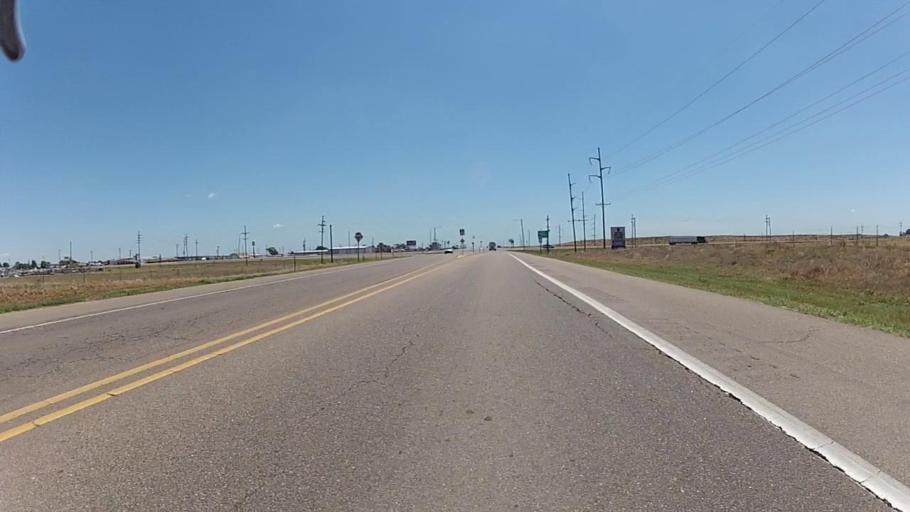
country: US
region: Kansas
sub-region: Ford County
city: Dodge City
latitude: 37.7217
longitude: -100.0169
